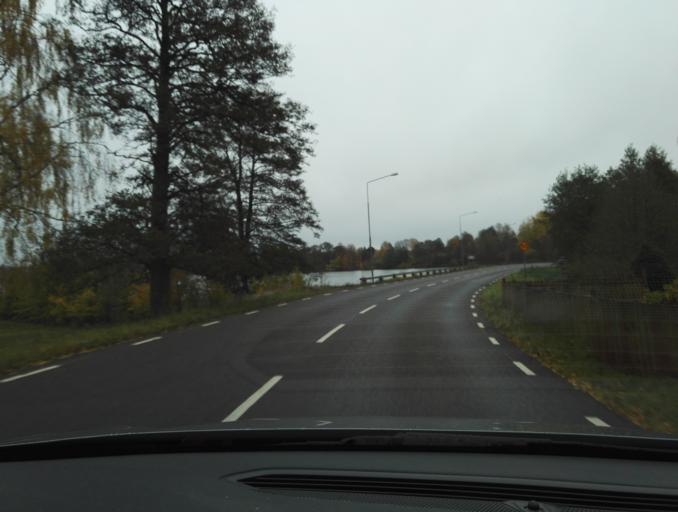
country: SE
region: Kronoberg
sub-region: Vaxjo Kommun
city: Rottne
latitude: 57.0260
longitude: 14.8754
